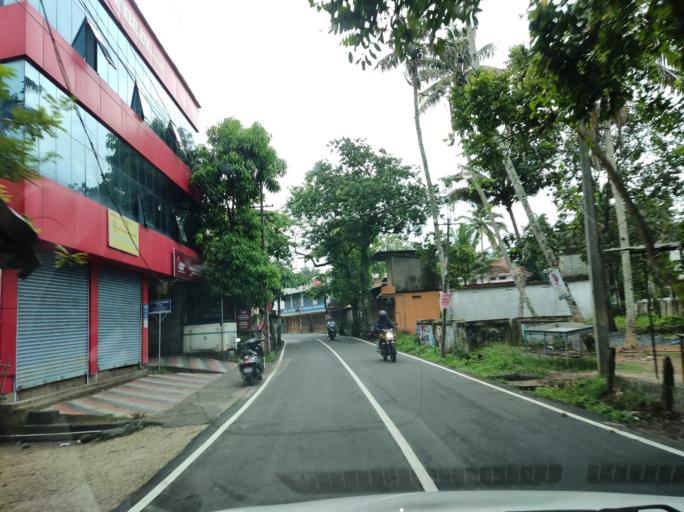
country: IN
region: Kerala
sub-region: Alappuzha
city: Kayankulam
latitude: 9.2603
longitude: 76.4092
